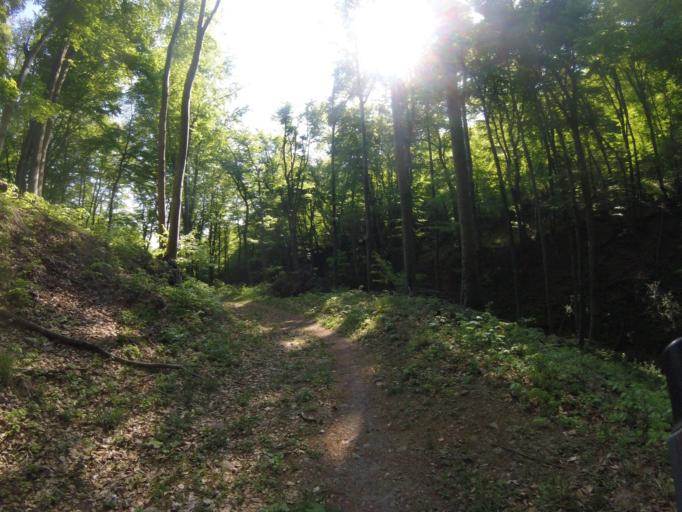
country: HU
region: Pest
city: Pilisszentkereszt
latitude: 47.7051
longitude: 18.8990
